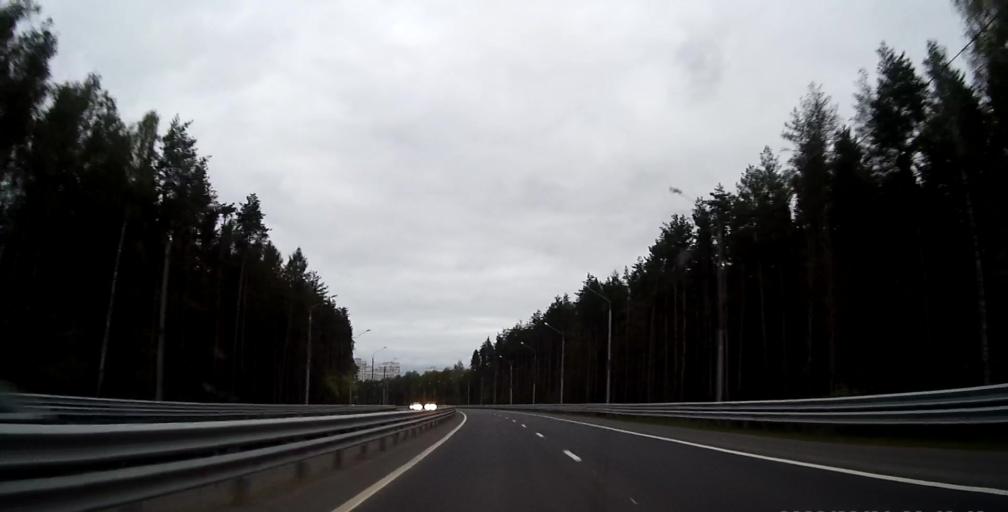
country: RU
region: Moskovskaya
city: Dubrovitsy
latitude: 55.4044
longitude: 37.5007
